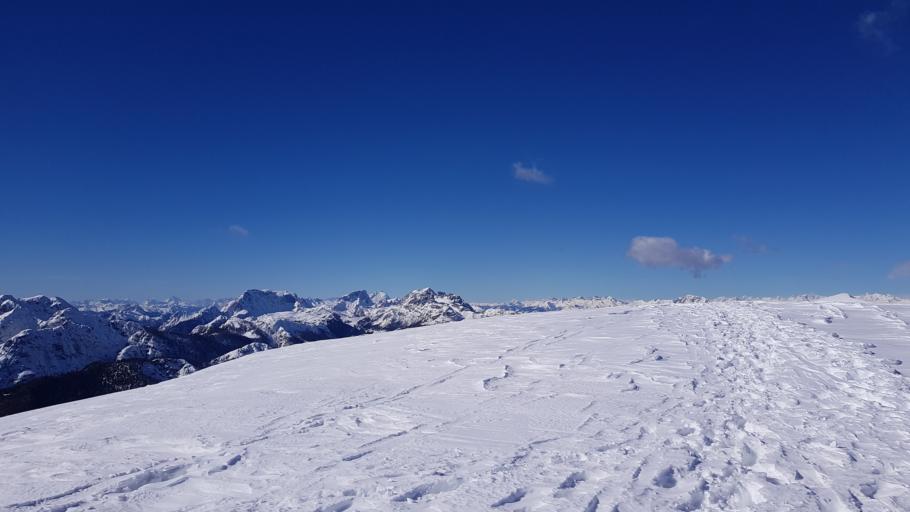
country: IT
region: Friuli Venezia Giulia
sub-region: Provincia di Udine
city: Malborghetto
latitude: 46.5496
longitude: 13.4432
